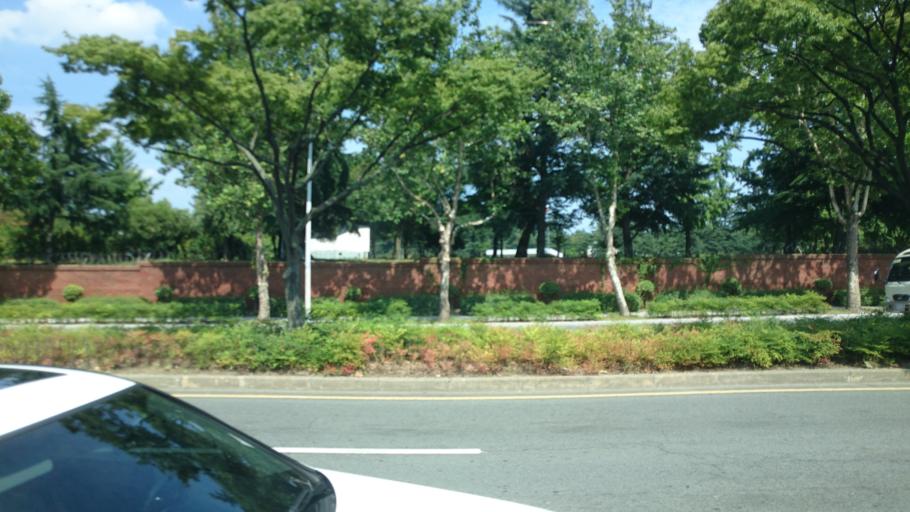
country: KR
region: Daegu
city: Daegu
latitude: 35.8706
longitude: 128.6486
